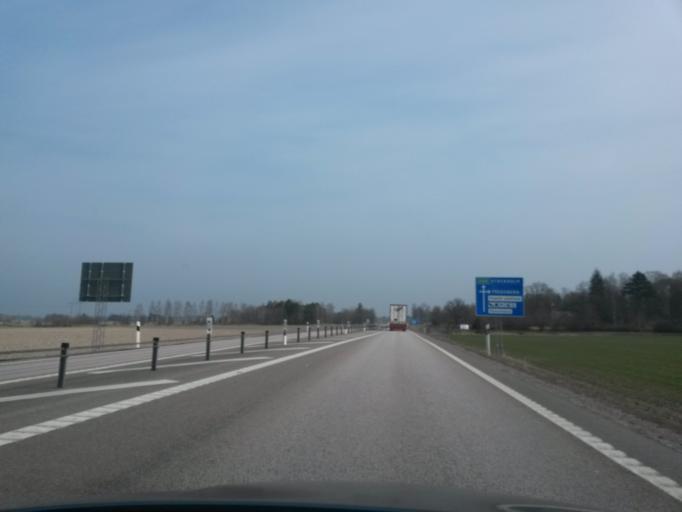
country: SE
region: Vaestra Goetaland
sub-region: Mariestads Kommun
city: Mariestad
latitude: 58.7480
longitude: 13.9518
